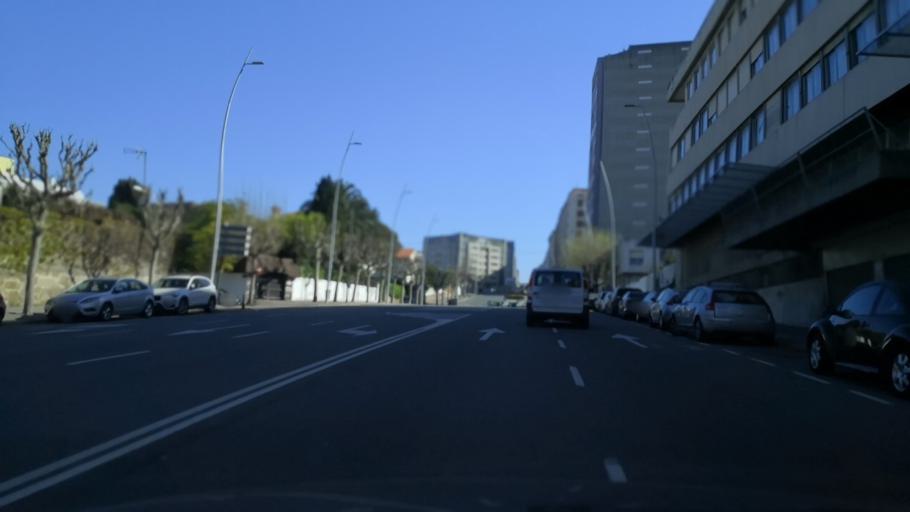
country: ES
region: Galicia
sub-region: Provincia da Coruna
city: A Coruna
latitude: 43.3672
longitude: -8.4205
